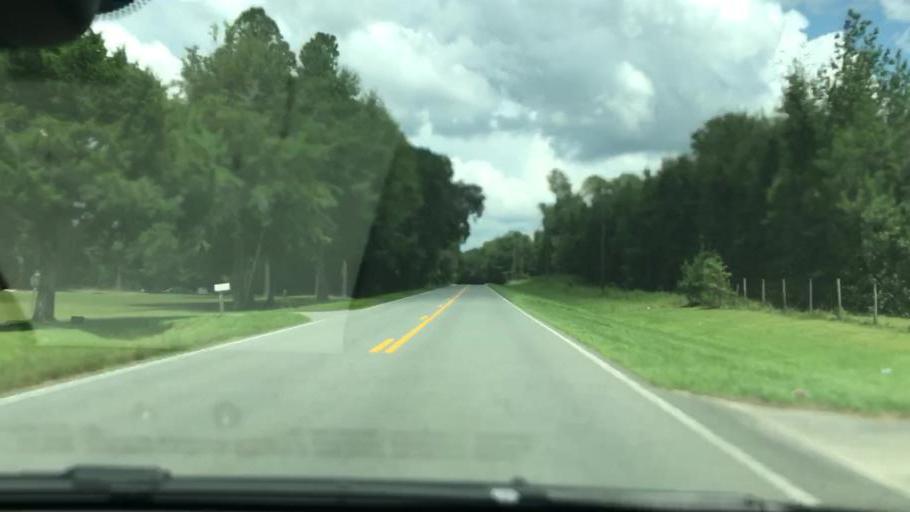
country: US
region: Florida
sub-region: Jackson County
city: Malone
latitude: 30.9072
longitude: -85.1249
